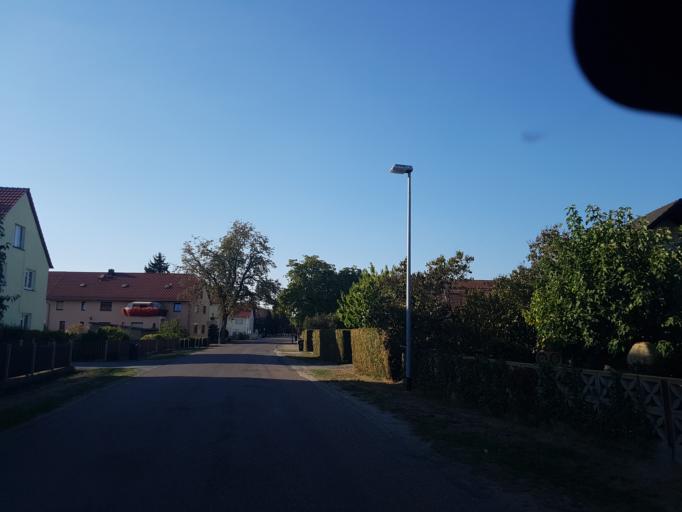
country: DE
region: Saxony
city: Nauwalde
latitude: 51.4460
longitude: 13.3931
